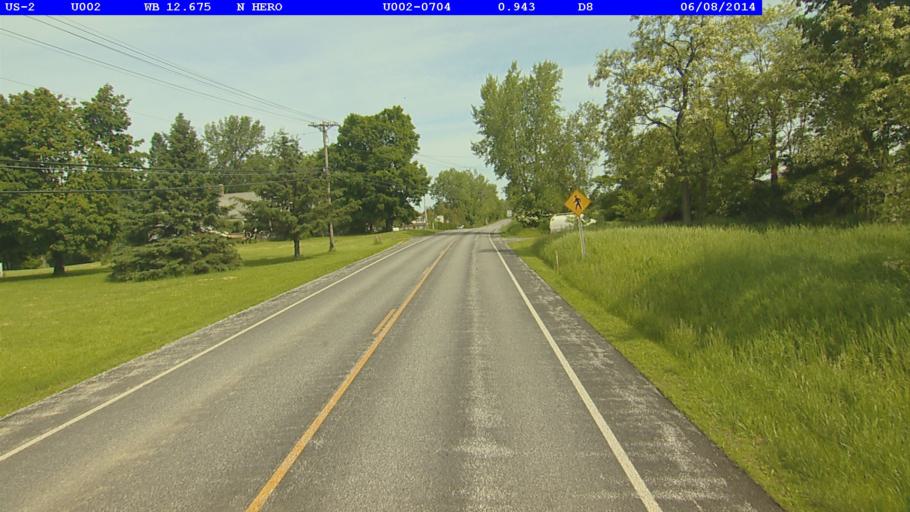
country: US
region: Vermont
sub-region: Grand Isle County
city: North Hero
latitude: 44.8729
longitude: -73.2709
